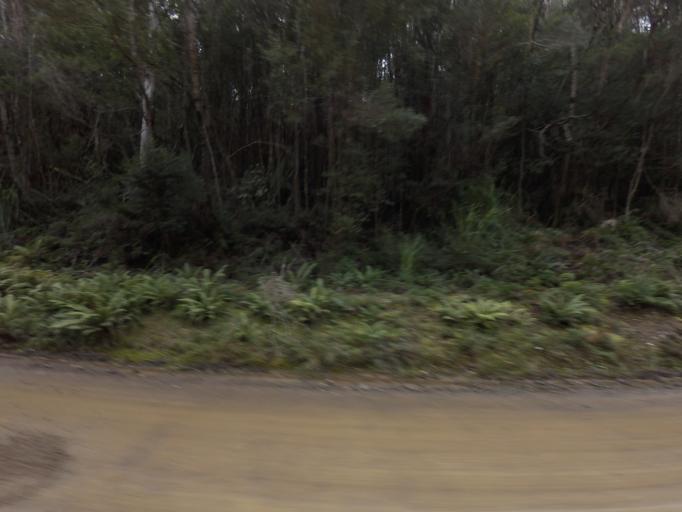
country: AU
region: Tasmania
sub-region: Huon Valley
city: Geeveston
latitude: -43.4079
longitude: 146.8699
